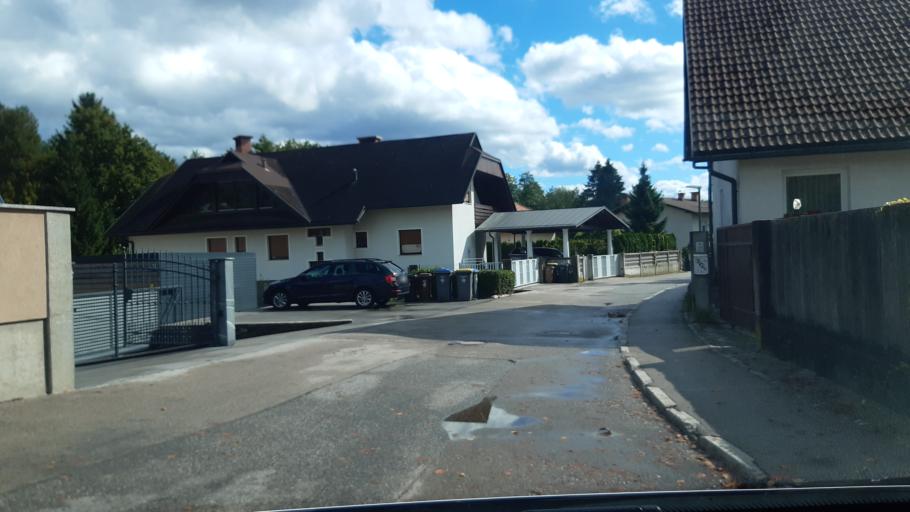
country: SI
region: Trzin
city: Trzin
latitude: 46.1076
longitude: 14.5287
